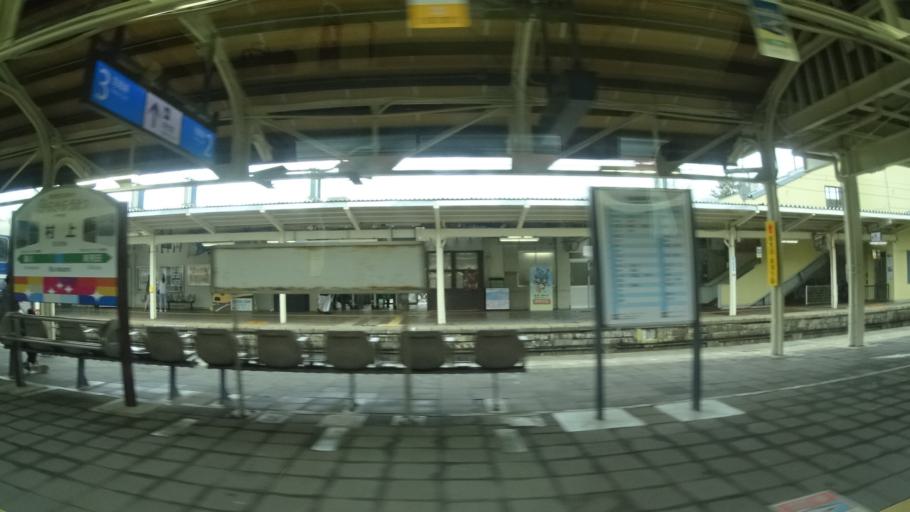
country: JP
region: Niigata
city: Murakami
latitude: 38.2202
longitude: 139.4634
